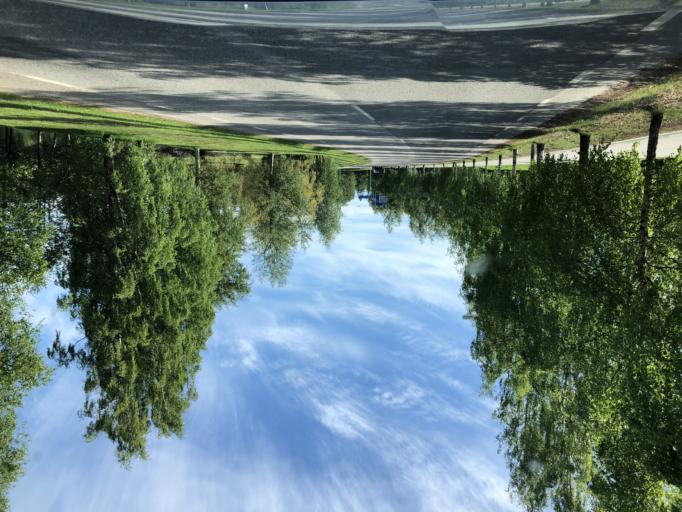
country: SE
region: Norrbotten
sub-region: Pitea Kommun
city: Pitea
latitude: 65.3133
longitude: 21.4918
